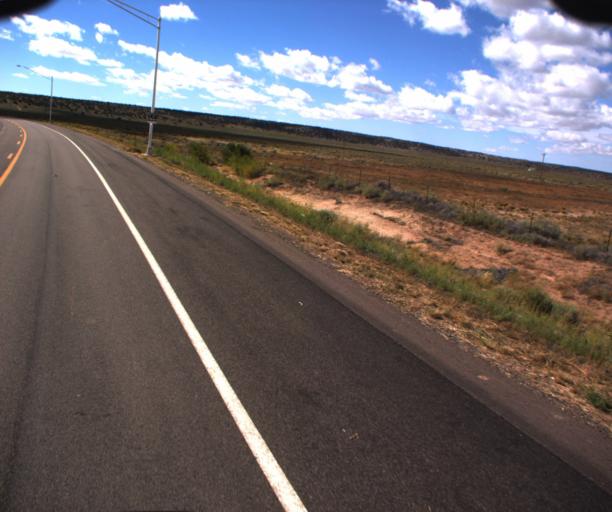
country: US
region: Arizona
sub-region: Apache County
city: Houck
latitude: 35.2055
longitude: -109.3323
